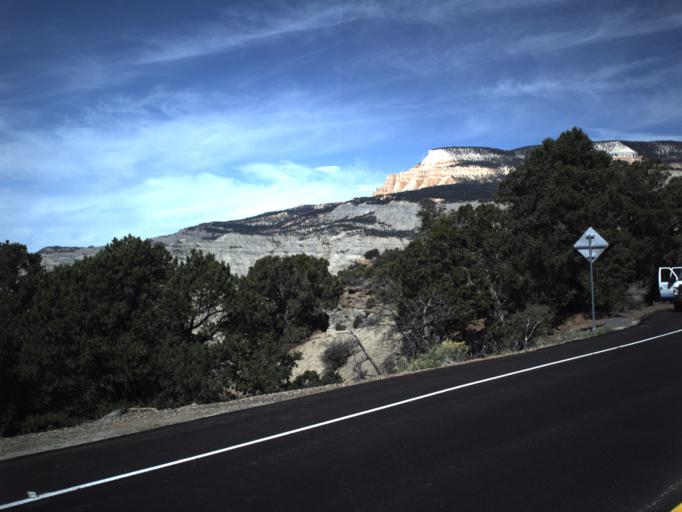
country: US
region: Utah
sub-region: Garfield County
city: Panguitch
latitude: 37.6389
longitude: -111.8439
